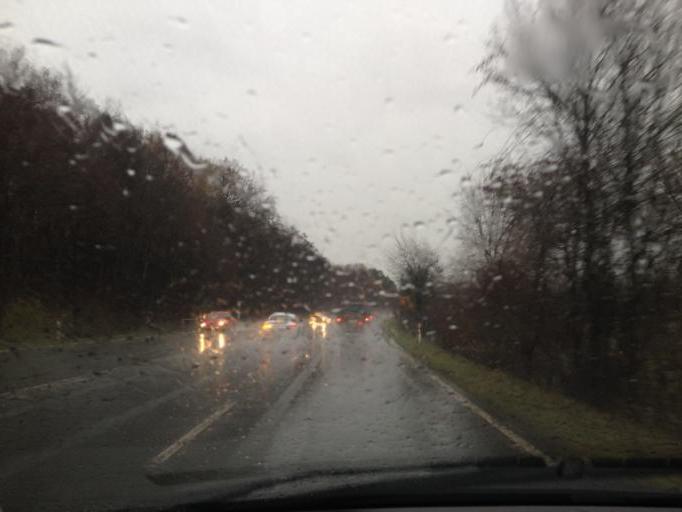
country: DE
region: Bavaria
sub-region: Regierungsbezirk Mittelfranken
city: Ruckersdorf
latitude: 49.5010
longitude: 11.2552
